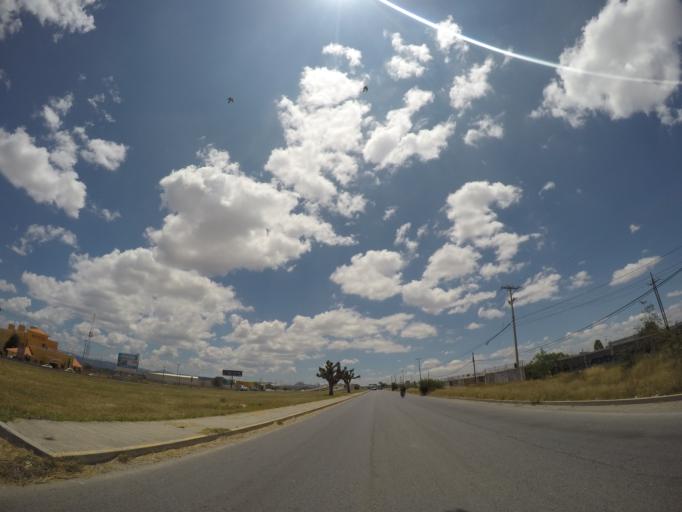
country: MX
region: San Luis Potosi
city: La Pila
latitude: 22.0463
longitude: -100.8585
